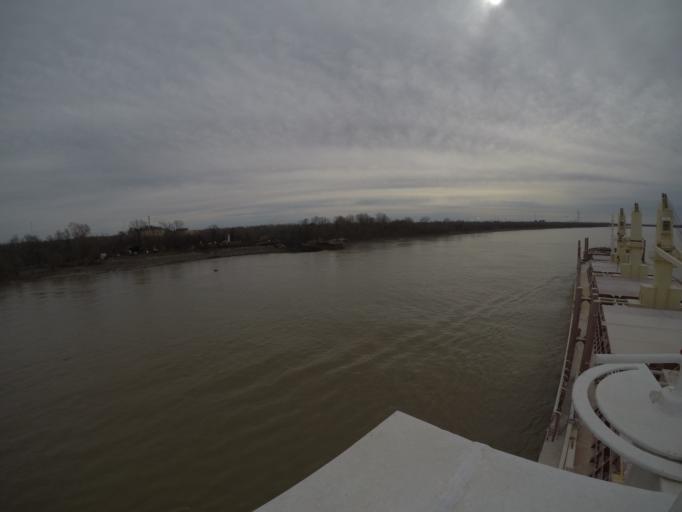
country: US
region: Louisiana
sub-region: Saint John the Baptist Parish
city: Laplace
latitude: 30.0373
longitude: -90.4722
